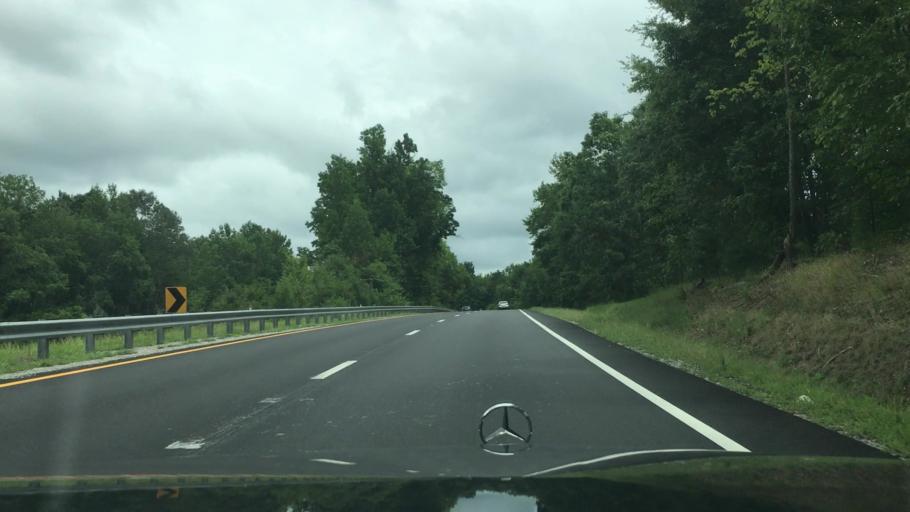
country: US
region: Virginia
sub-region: Prince Edward County
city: Farmville
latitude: 37.2746
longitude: -78.3123
